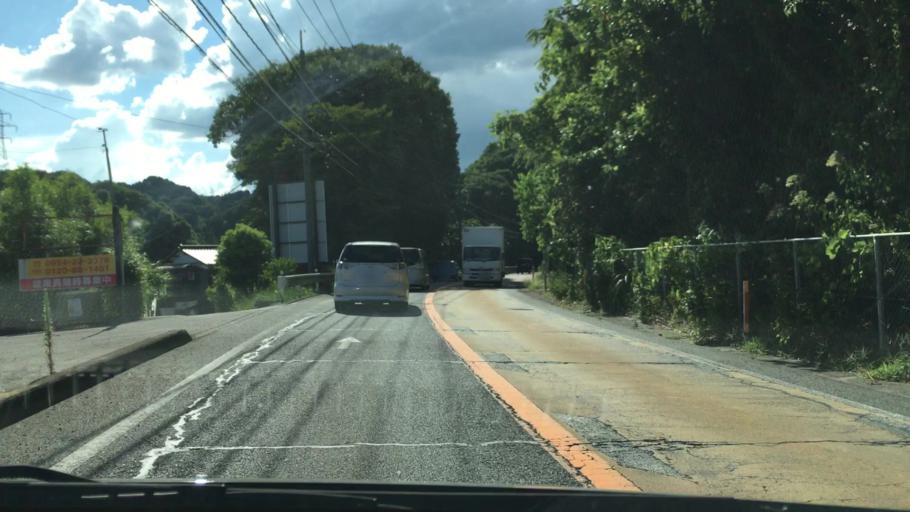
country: JP
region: Saga Prefecture
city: Takeocho-takeo
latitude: 33.1840
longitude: 129.9934
